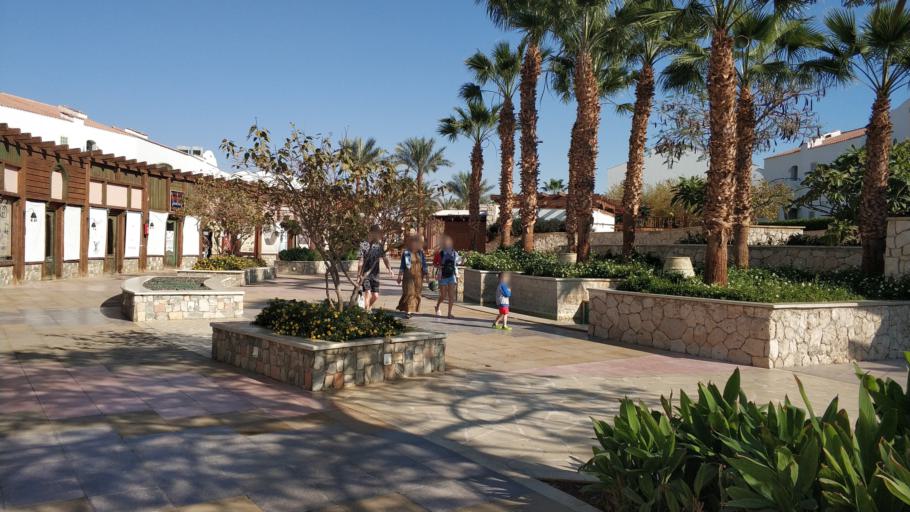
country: EG
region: South Sinai
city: Sharm el-Sheikh
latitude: 27.9172
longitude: 34.3614
